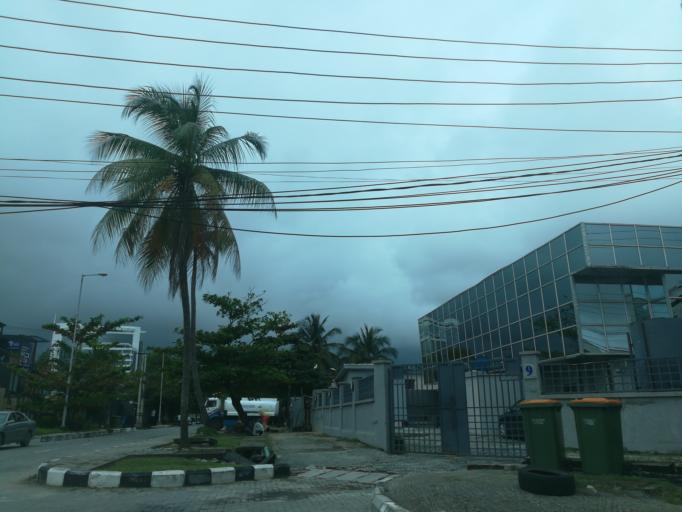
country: NG
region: Lagos
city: Ikoyi
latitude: 6.4252
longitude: 3.4192
